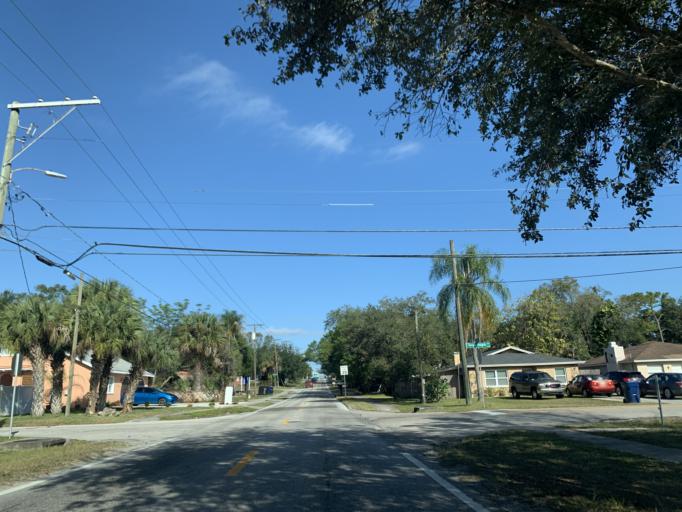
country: US
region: Florida
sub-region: Hillsborough County
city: Temple Terrace
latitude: 28.0360
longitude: -82.4099
